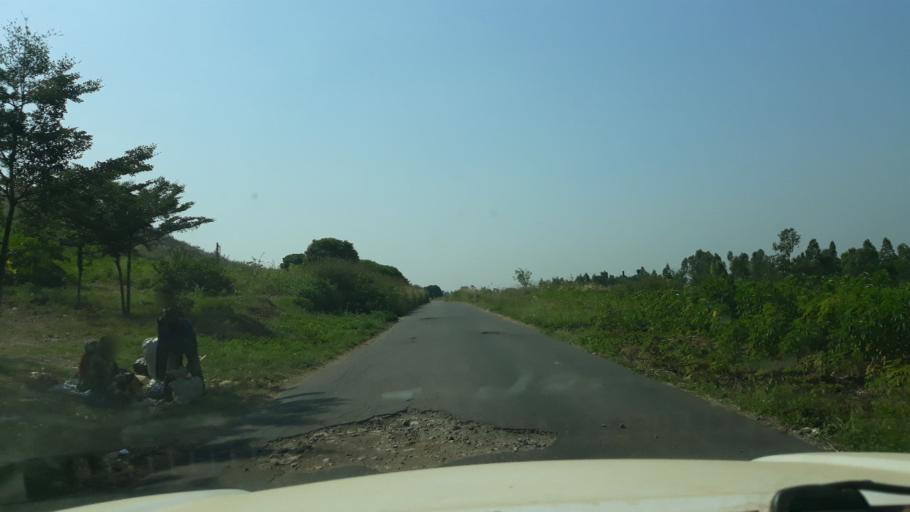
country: CD
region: South Kivu
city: Uvira
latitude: -3.2692
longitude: 29.1614
